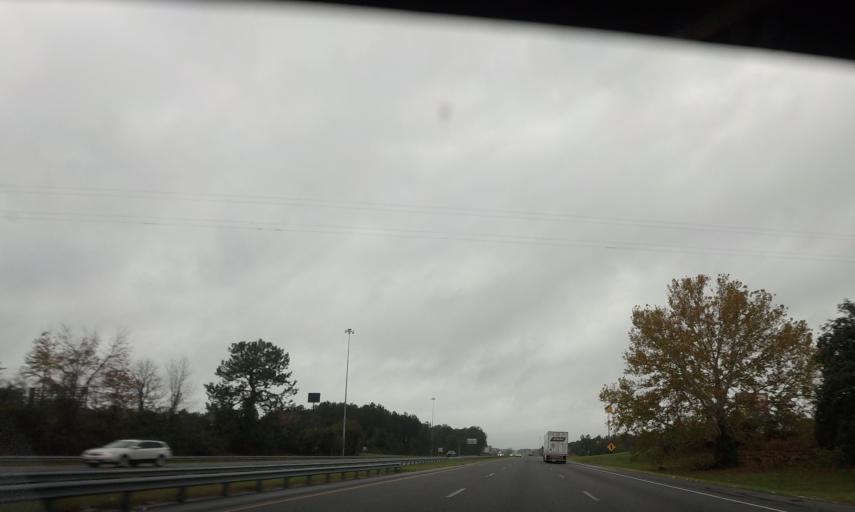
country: US
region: Georgia
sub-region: Echols County
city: Statenville
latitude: 30.6438
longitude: -83.1892
